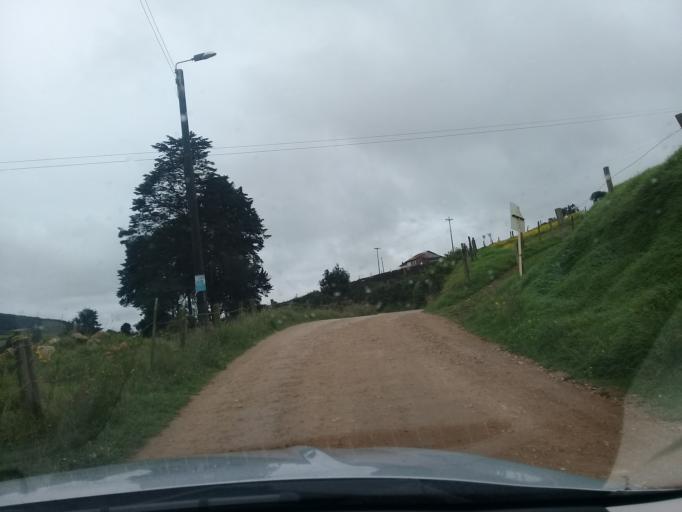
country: CO
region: Boyaca
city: Samaca
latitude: 5.4486
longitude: -73.4366
